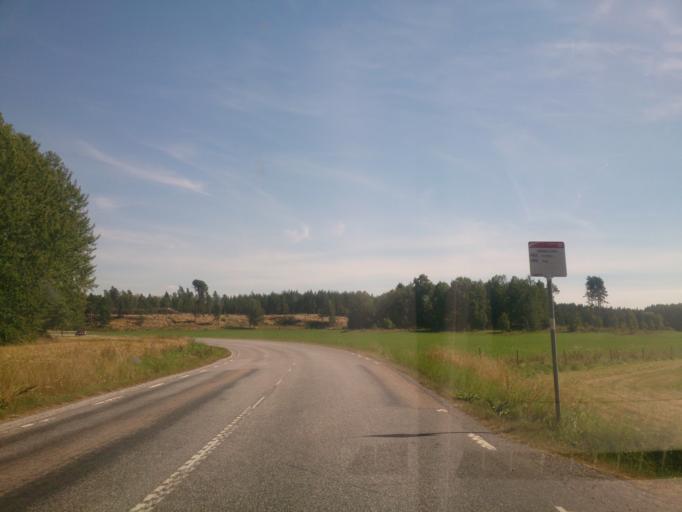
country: SE
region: OEstergoetland
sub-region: Norrkopings Kommun
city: Kimstad
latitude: 58.4804
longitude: 16.0111
